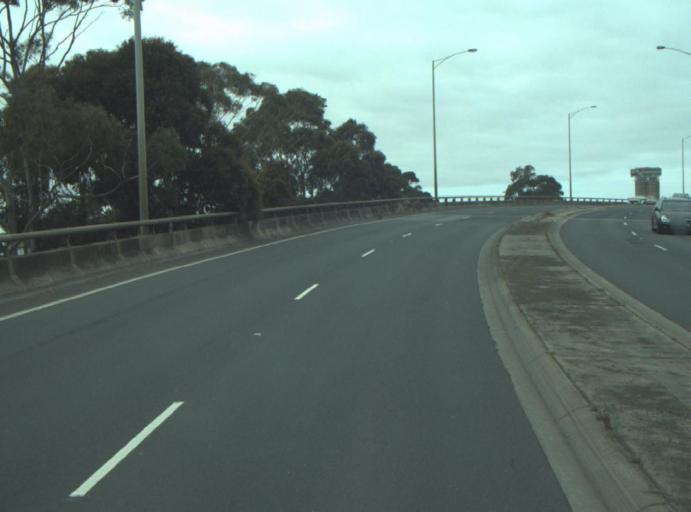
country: AU
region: Victoria
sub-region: Greater Geelong
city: Geelong West
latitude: -38.1377
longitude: 144.3535
